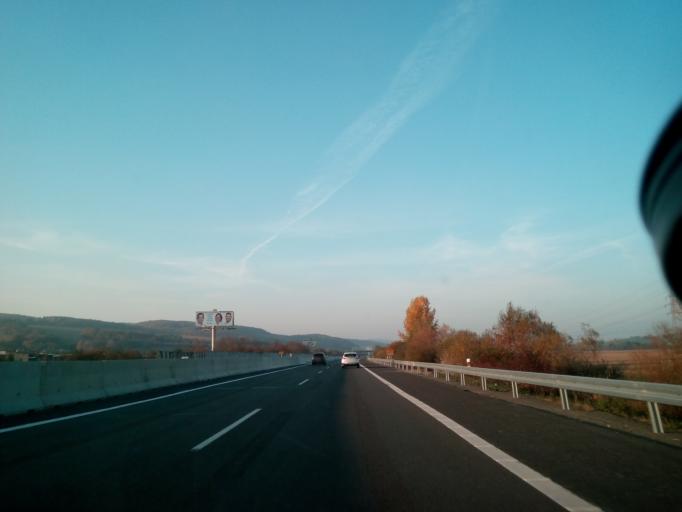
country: SK
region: Presovsky
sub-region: Okres Presov
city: Presov
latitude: 48.8719
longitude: 21.2547
